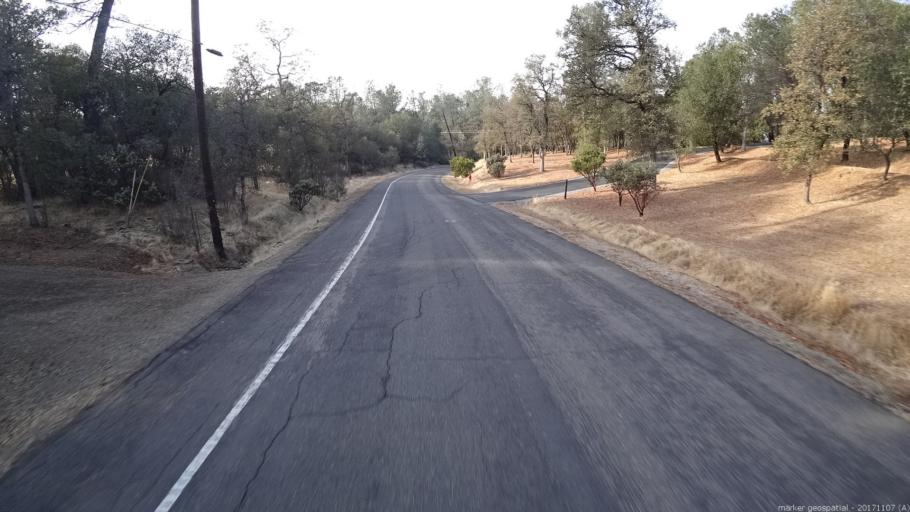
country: US
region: California
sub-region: Shasta County
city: Shasta
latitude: 40.5174
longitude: -122.4609
